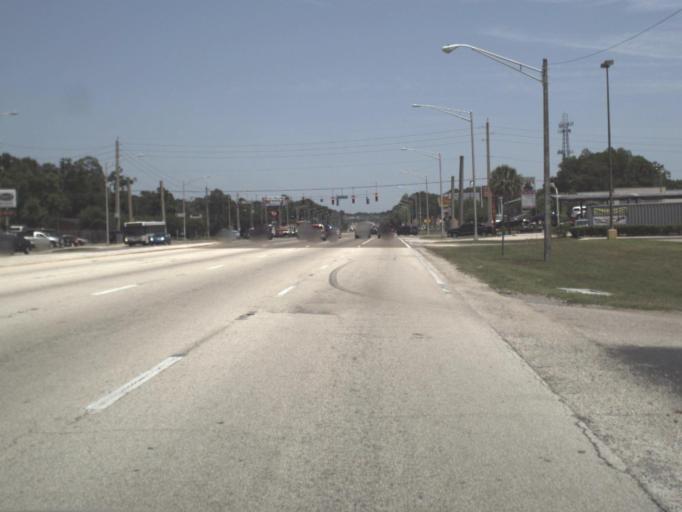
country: US
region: Florida
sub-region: Duval County
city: Jacksonville
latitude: 30.2886
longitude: -81.5798
